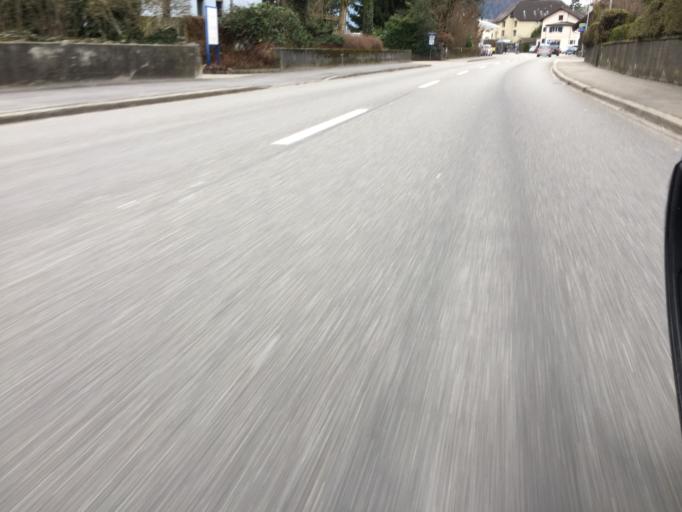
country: CH
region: Bern
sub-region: Emmental District
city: Burgdorf
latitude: 47.0527
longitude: 7.6239
